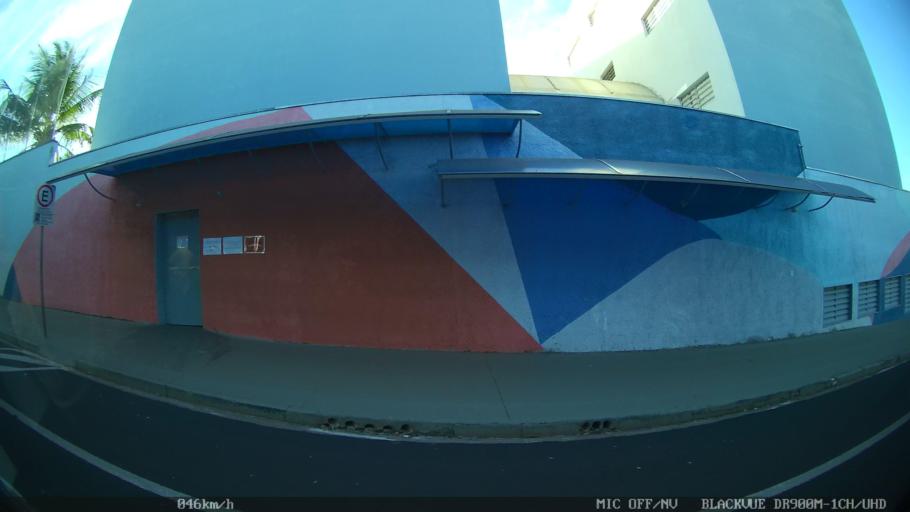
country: BR
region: Sao Paulo
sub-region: Sao Jose Do Rio Preto
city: Sao Jose do Rio Preto
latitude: -20.8261
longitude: -49.3692
